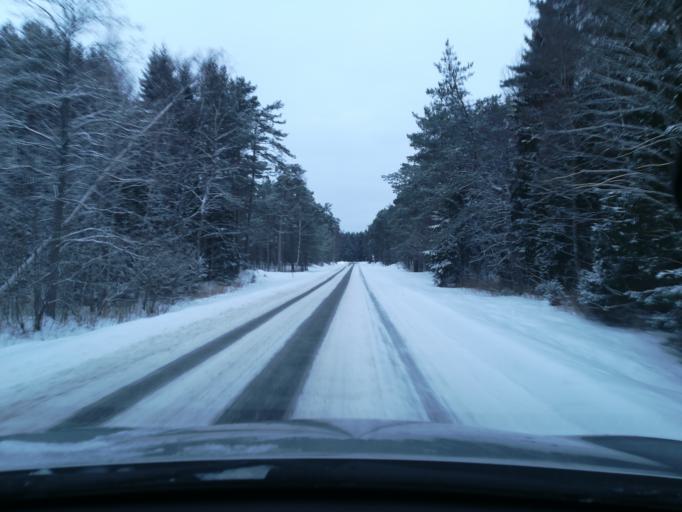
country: EE
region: Harju
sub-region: Keila linn
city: Keila
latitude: 59.3900
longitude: 24.2953
